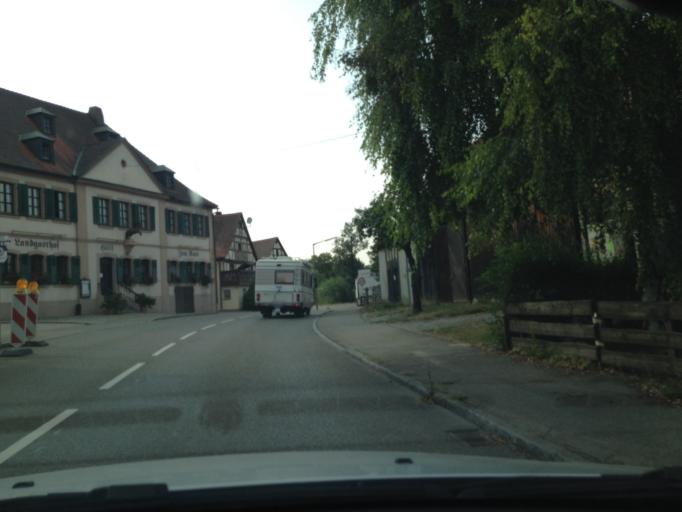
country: DE
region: Bavaria
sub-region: Regierungsbezirk Mittelfranken
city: Dombuhl
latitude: 49.2154
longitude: 10.3020
